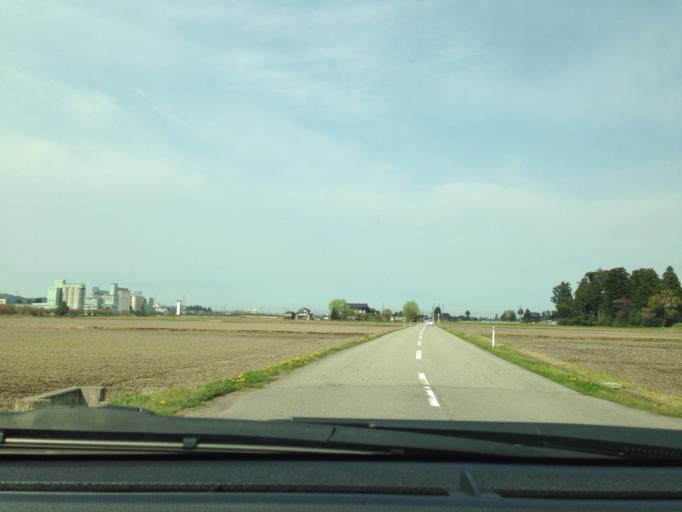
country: JP
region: Toyama
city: Fukumitsu
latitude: 36.5386
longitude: 136.8648
